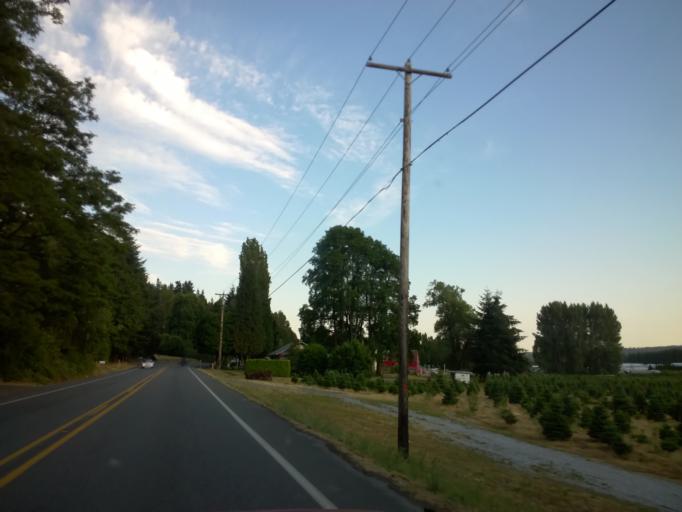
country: US
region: Washington
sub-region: King County
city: Woodinville
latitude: 47.7259
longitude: -122.1360
